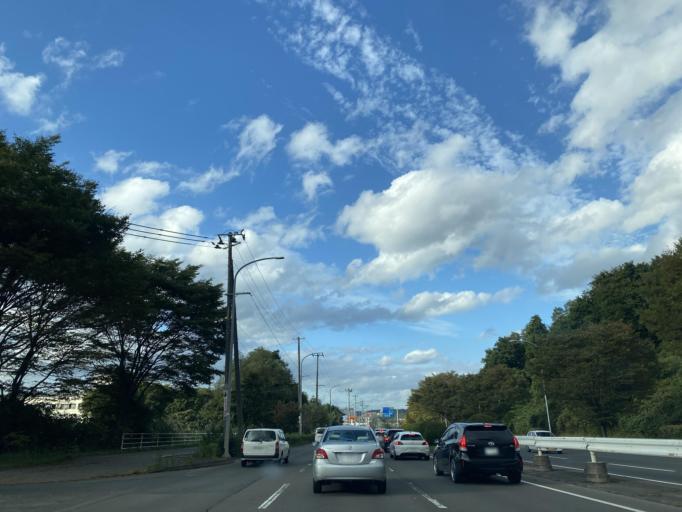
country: JP
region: Miyagi
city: Sendai-shi
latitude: 38.3153
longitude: 140.8447
